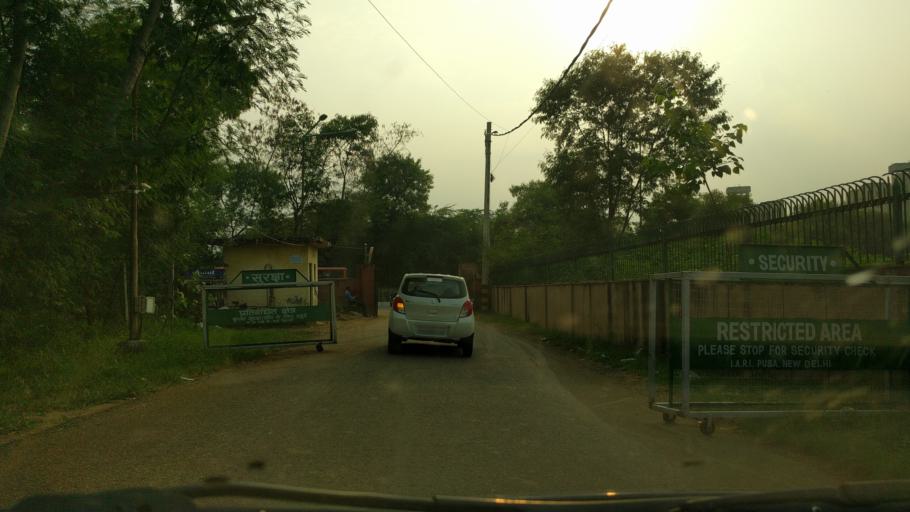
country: IN
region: NCT
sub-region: Central Delhi
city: Karol Bagh
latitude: 28.6276
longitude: 77.1529
